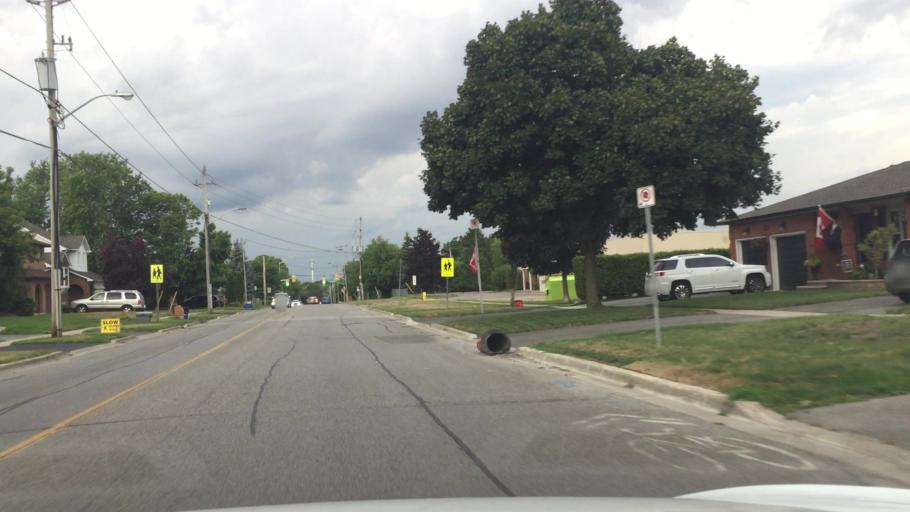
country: CA
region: Ontario
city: Oshawa
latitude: 43.9103
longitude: -78.8068
